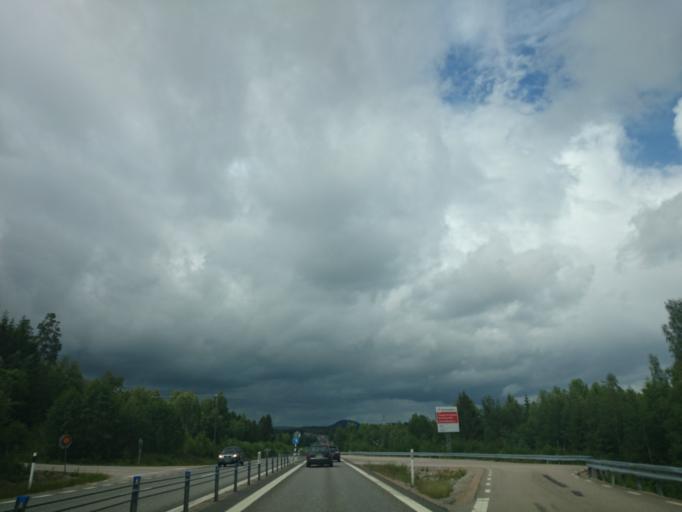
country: SE
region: Vaesternorrland
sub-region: Sundsvalls Kommun
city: Njurundabommen
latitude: 62.2392
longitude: 17.3745
